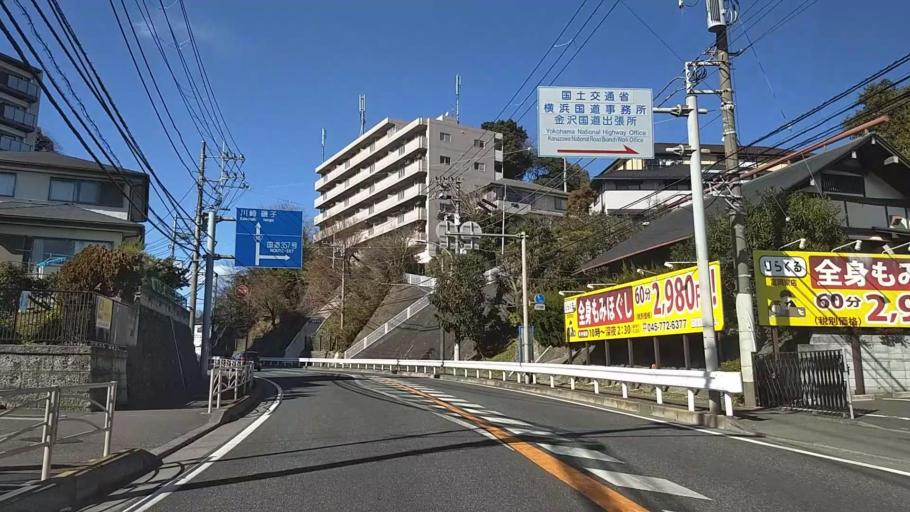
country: JP
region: Kanagawa
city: Yokohama
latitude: 35.3706
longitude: 139.6338
